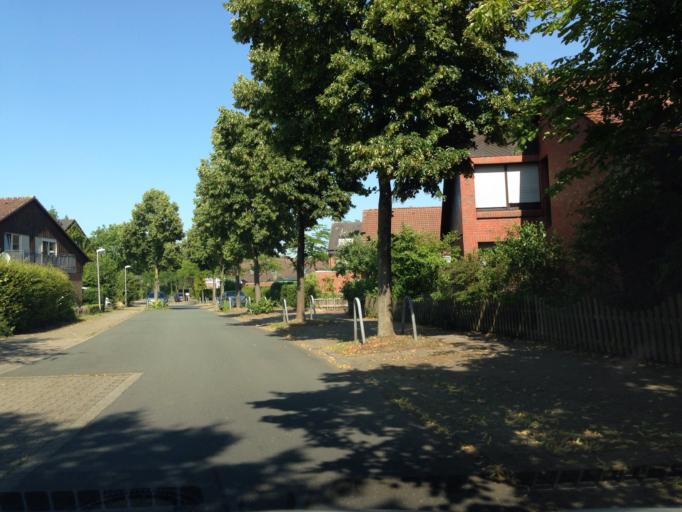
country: DE
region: North Rhine-Westphalia
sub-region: Regierungsbezirk Munster
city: Muenster
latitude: 51.9741
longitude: 7.5593
